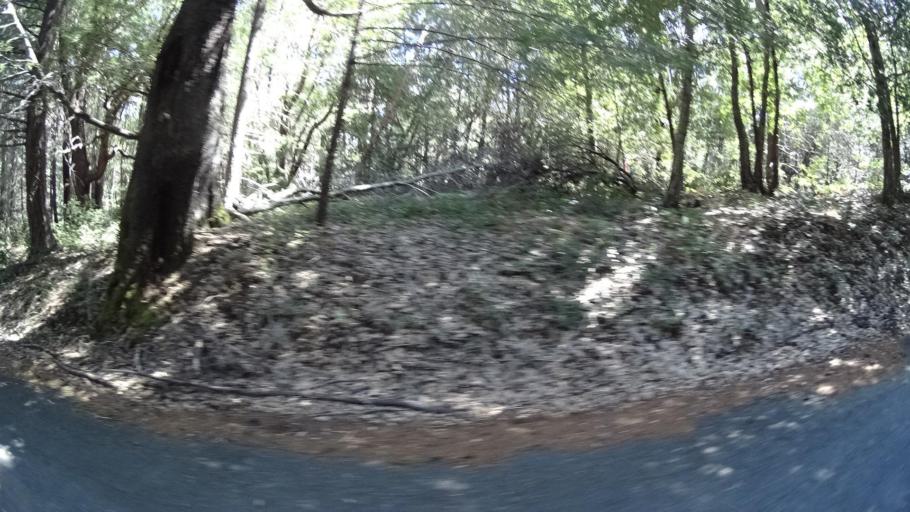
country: US
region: California
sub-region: Humboldt County
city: Redway
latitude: 40.1654
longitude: -124.0828
